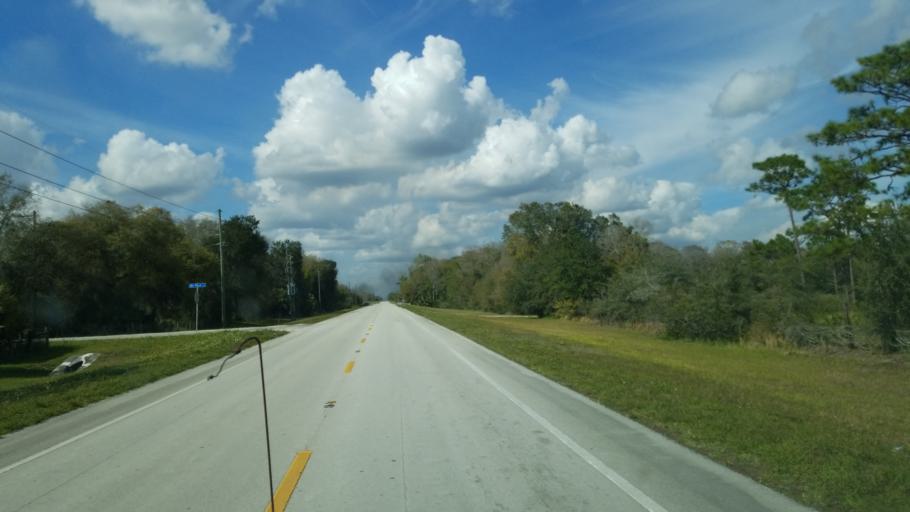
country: US
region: Florida
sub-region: Osceola County
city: Saint Cloud
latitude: 28.0267
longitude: -81.0377
